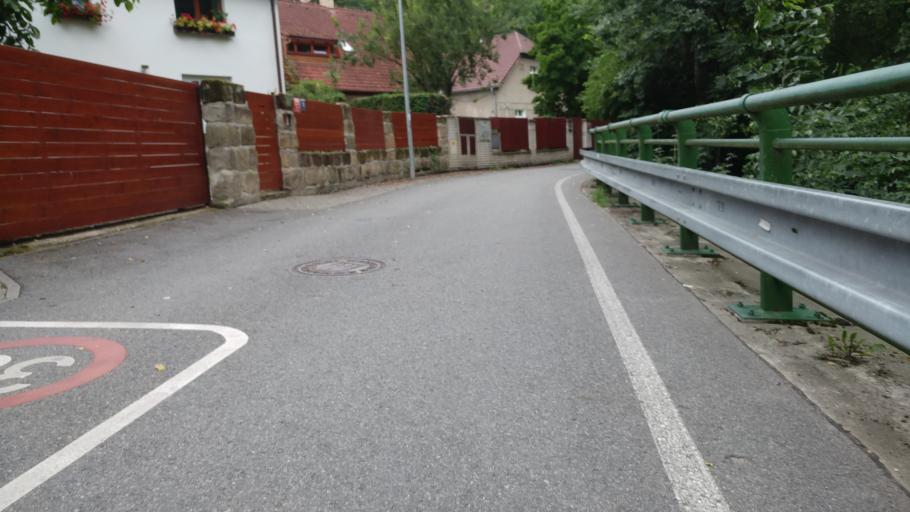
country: CZ
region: Central Bohemia
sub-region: Okres Praha-Zapad
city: Pruhonice
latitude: 50.0474
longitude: 14.5334
